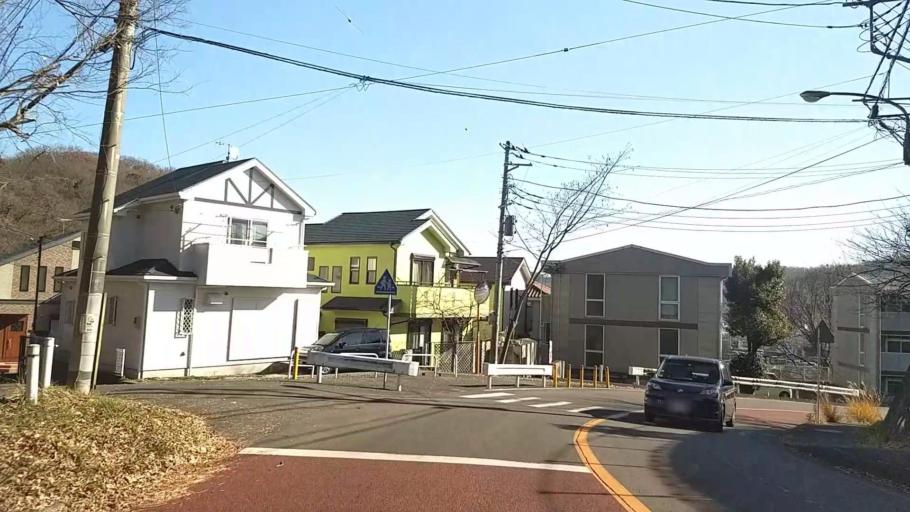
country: JP
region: Kanagawa
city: Hadano
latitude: 35.3824
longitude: 139.2263
